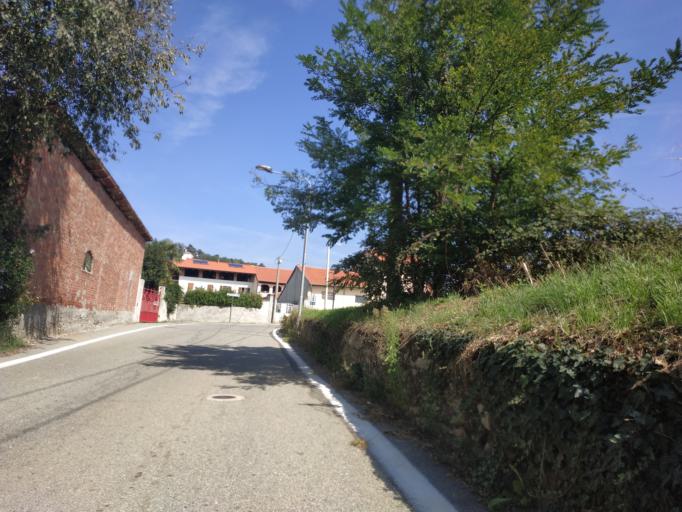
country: IT
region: Piedmont
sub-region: Provincia di Torino
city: Orio Canavese
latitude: 45.3250
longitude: 7.8592
